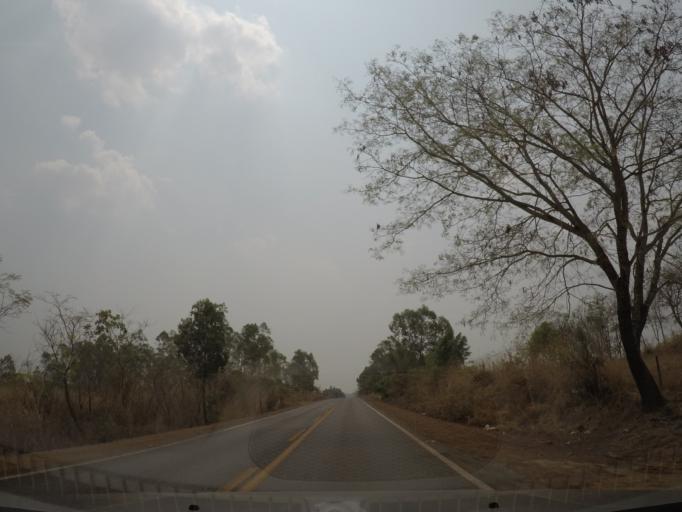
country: BR
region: Goias
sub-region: Pirenopolis
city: Pirenopolis
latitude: -15.9107
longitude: -48.8609
